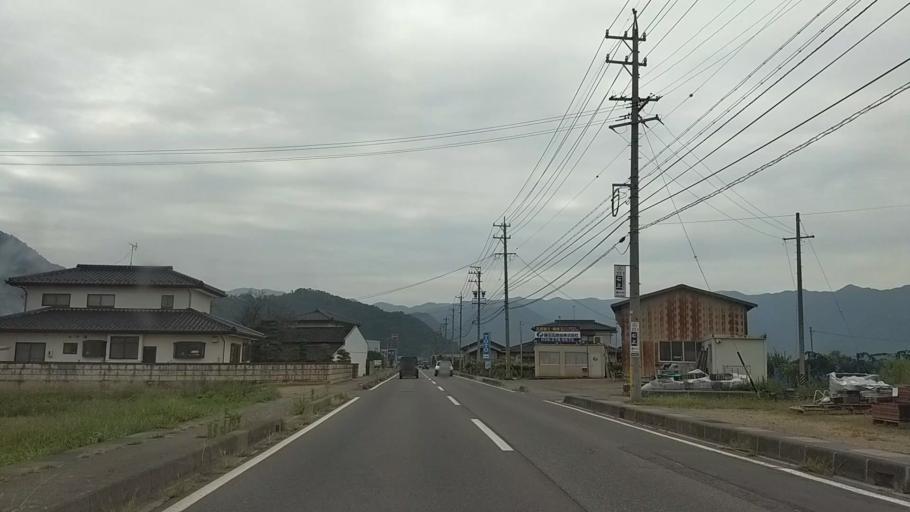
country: JP
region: Nagano
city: Nagano-shi
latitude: 36.5851
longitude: 138.1996
